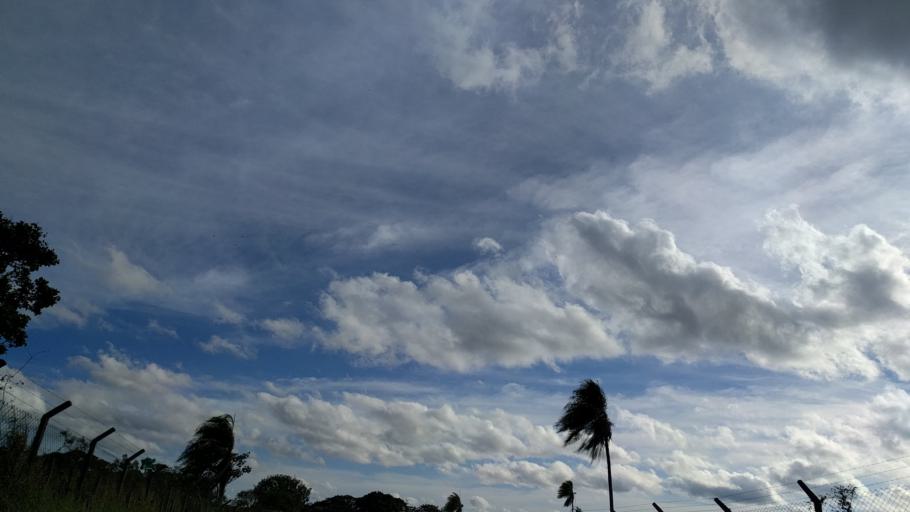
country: BO
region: Santa Cruz
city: Santa Cruz de la Sierra
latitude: -17.8543
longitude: -63.2648
